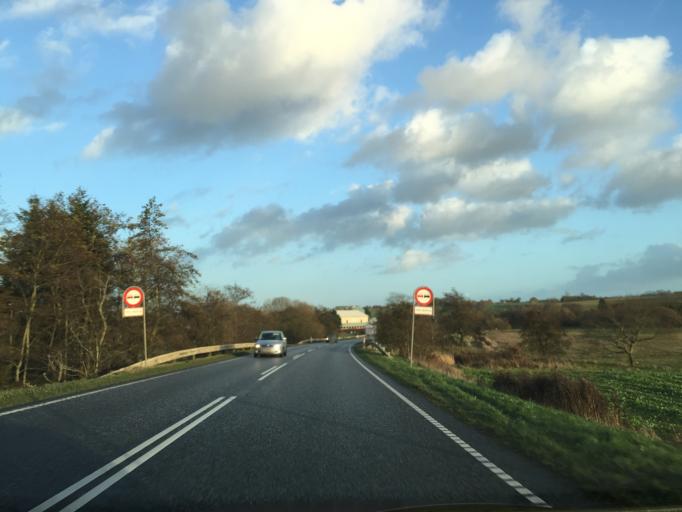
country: DK
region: Central Jutland
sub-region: Silkeborg Kommune
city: Kjellerup
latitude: 56.3035
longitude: 9.4664
